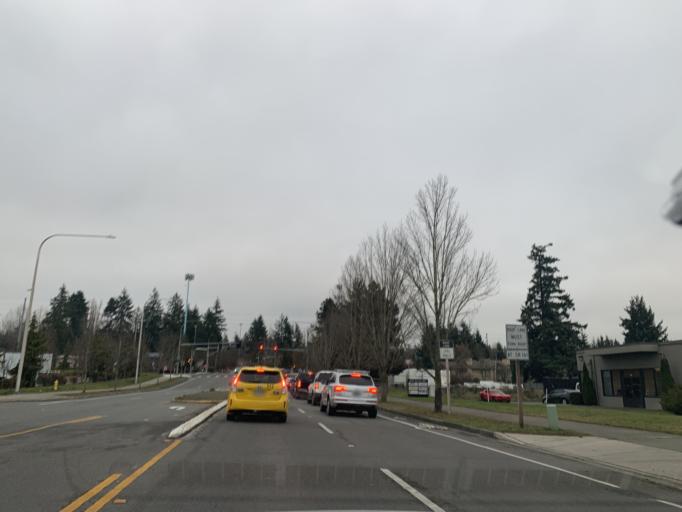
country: US
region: Washington
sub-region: King County
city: Lakeland South
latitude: 47.2826
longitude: -122.3152
